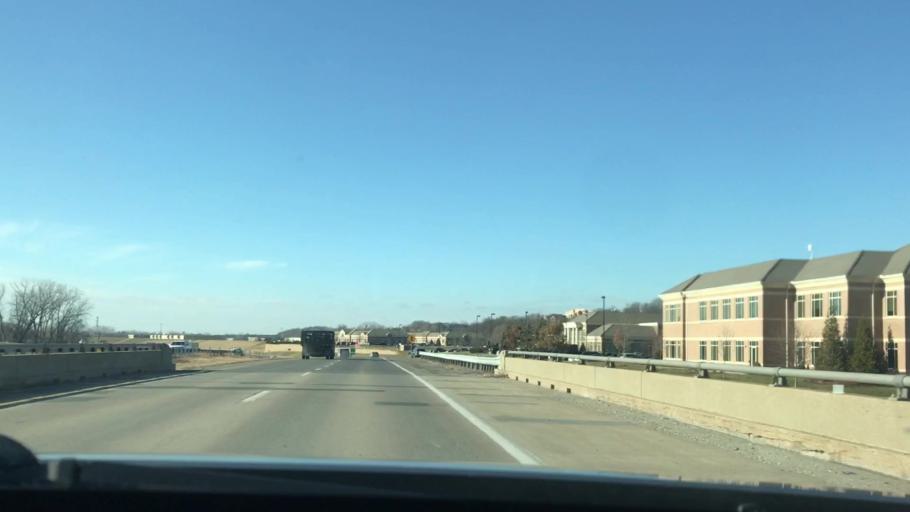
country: US
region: Missouri
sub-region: Platte County
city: Riverside
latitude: 39.1655
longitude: -94.5989
